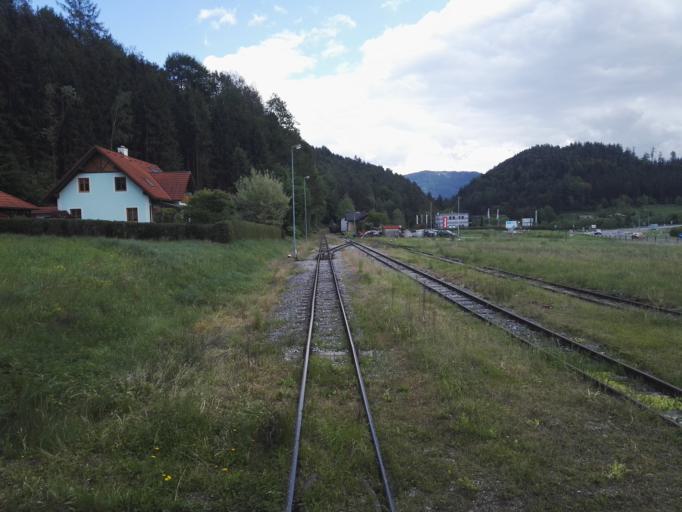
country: AT
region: Styria
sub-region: Politischer Bezirk Weiz
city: Baierdorf-Umgebung
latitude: 47.2618
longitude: 15.7129
